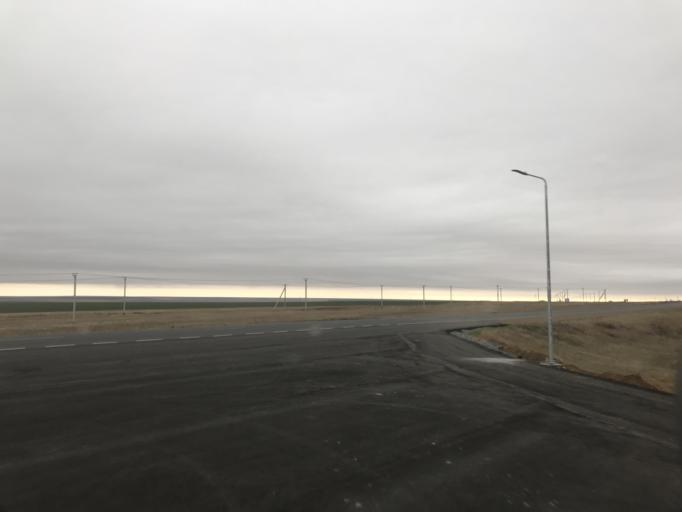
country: KZ
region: Batys Qazaqstan
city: Peremetnoe
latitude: 51.6465
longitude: 51.0122
